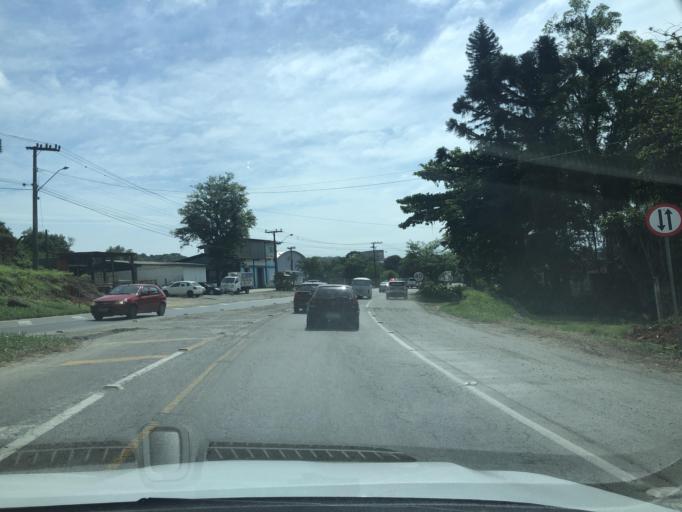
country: BR
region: Santa Catarina
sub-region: Sao Francisco Do Sul
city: Sao Francisco do Sul
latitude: -26.2533
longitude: -48.6132
